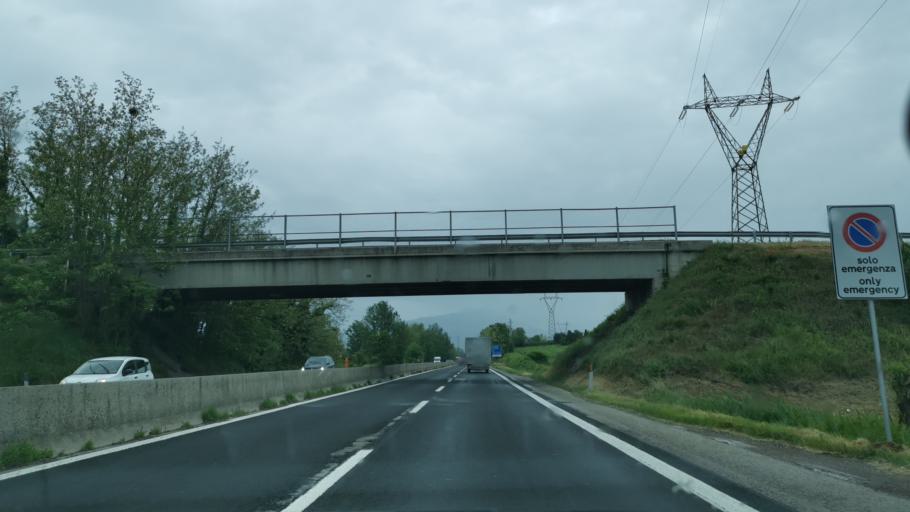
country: IT
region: Veneto
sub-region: Provincia di Verona
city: Cola
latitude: 45.4841
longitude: 10.7655
